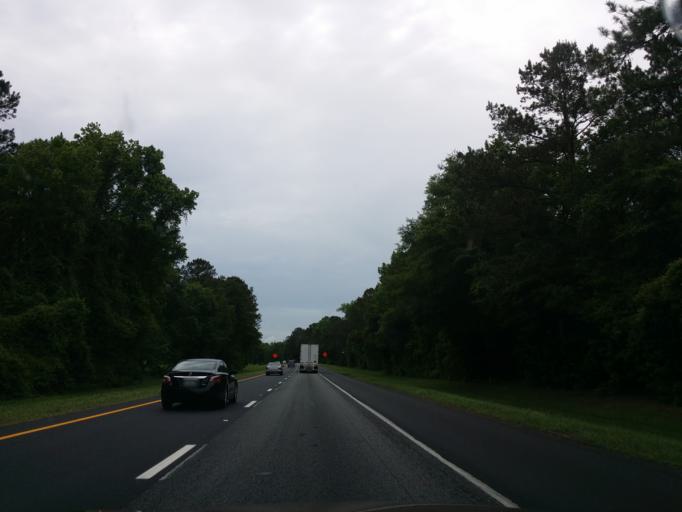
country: US
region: Florida
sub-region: Jefferson County
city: Monticello
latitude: 30.4434
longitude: -83.6704
